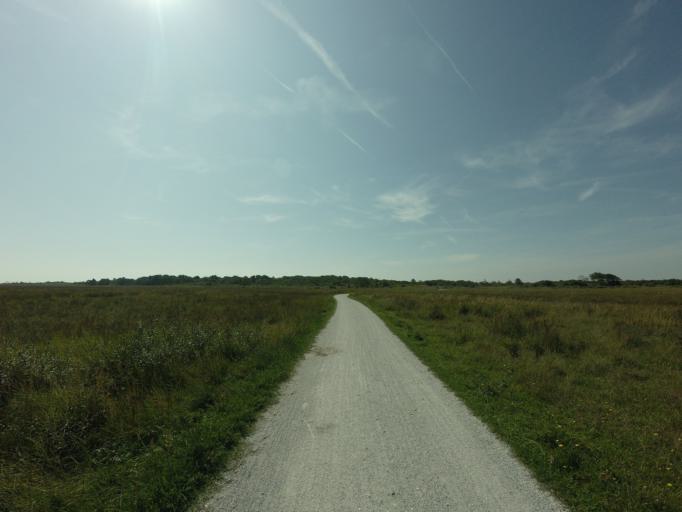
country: NL
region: Friesland
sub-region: Gemeente Schiermonnikoog
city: Schiermonnikoog
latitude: 53.4860
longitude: 6.2057
